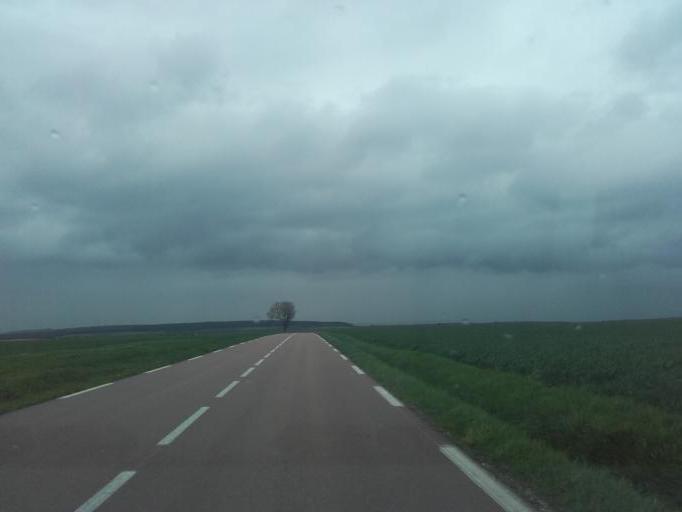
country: FR
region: Bourgogne
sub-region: Departement de l'Yonne
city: Joux-la-Ville
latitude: 47.7150
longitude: 3.8527
